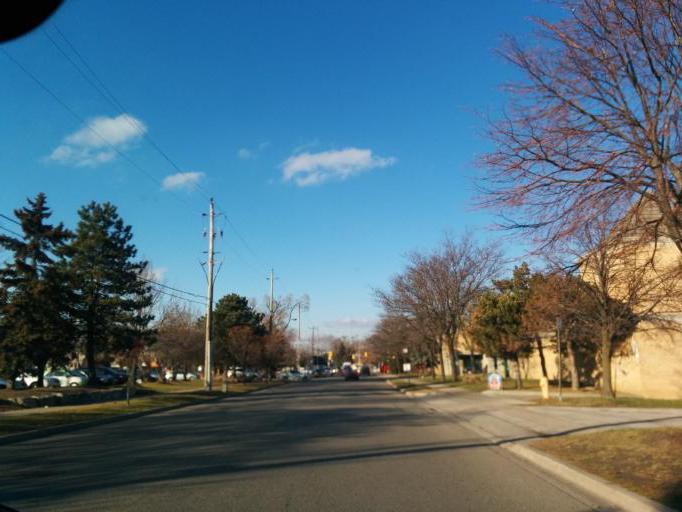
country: CA
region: Ontario
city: Etobicoke
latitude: 43.6237
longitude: -79.5065
